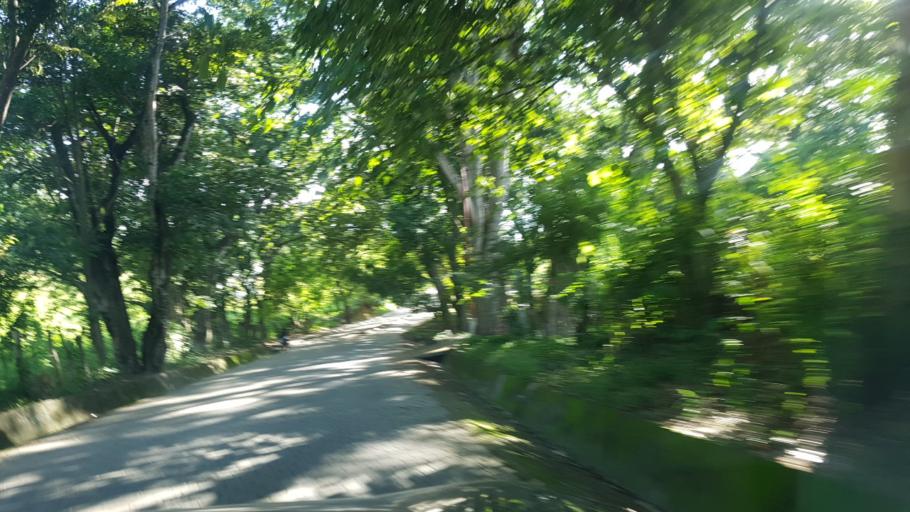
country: NI
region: Nueva Segovia
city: Mozonte
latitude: 13.6523
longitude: -86.4409
